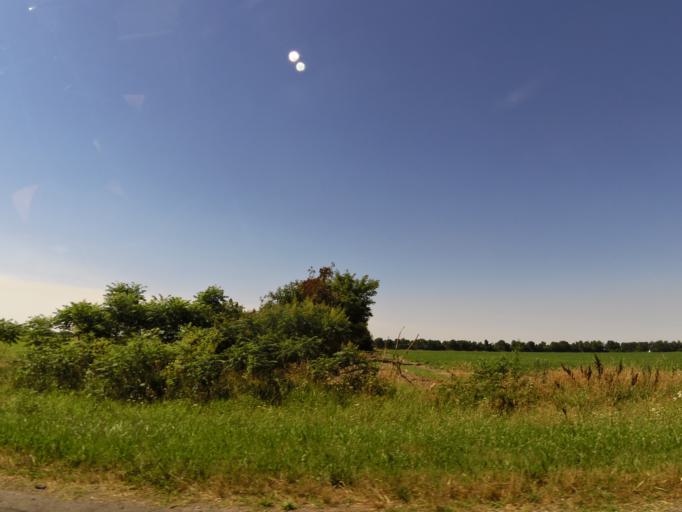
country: US
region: Missouri
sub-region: Dunklin County
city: Campbell
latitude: 36.4917
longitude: -90.0492
